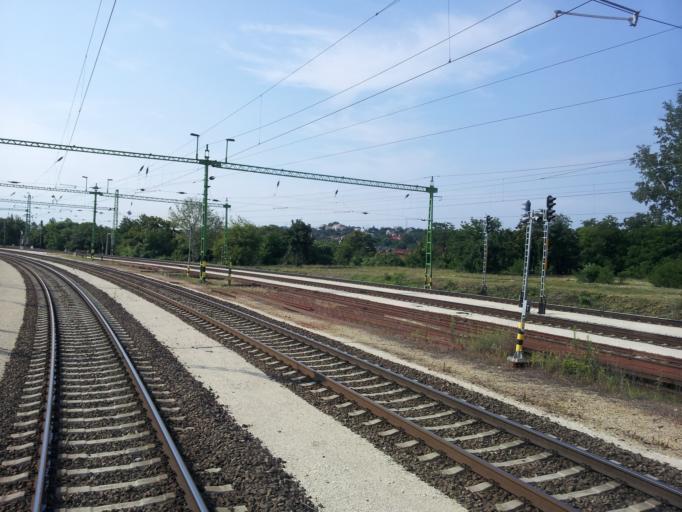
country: HU
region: Budapest
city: Budapest XI. keruelet
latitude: 47.4559
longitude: 19.0216
